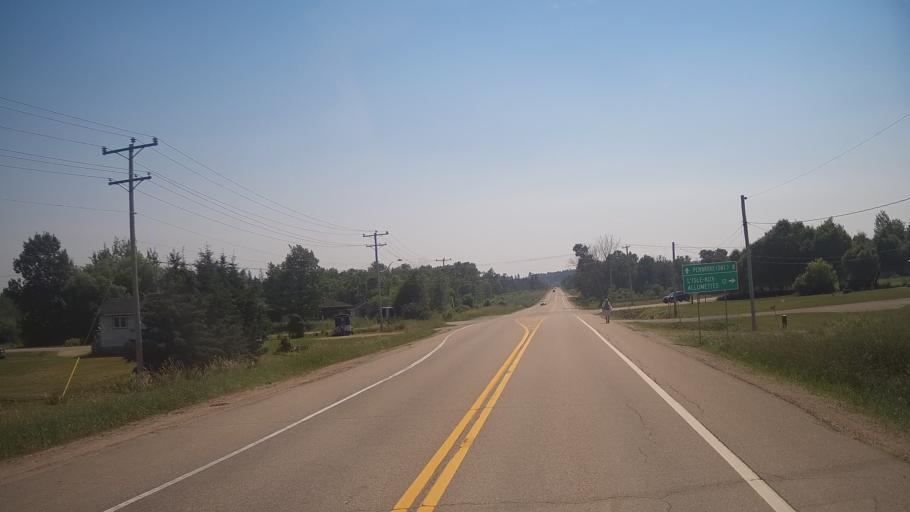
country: CA
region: Ontario
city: Pembroke
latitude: 45.8268
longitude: -77.0155
